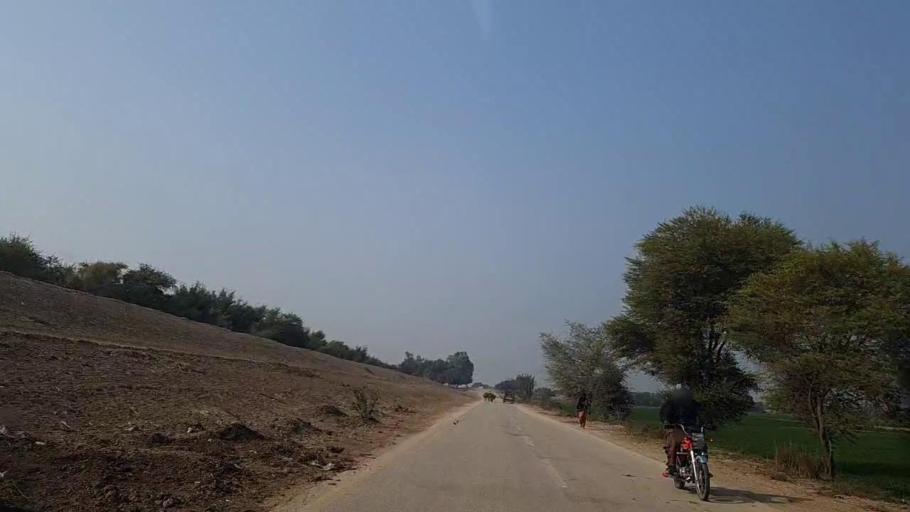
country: PK
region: Sindh
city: Sann
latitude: 26.1645
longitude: 68.1119
